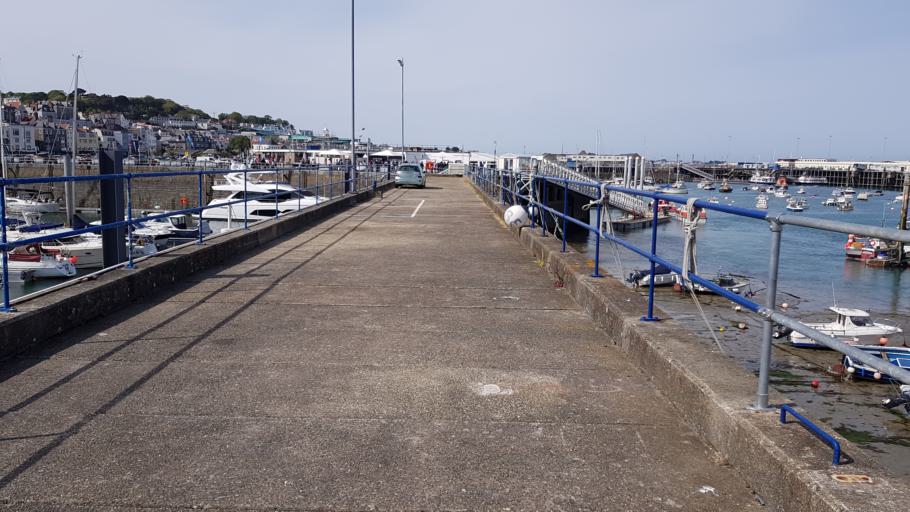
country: GG
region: St Peter Port
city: Saint Peter Port
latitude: 49.4533
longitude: -2.5333
